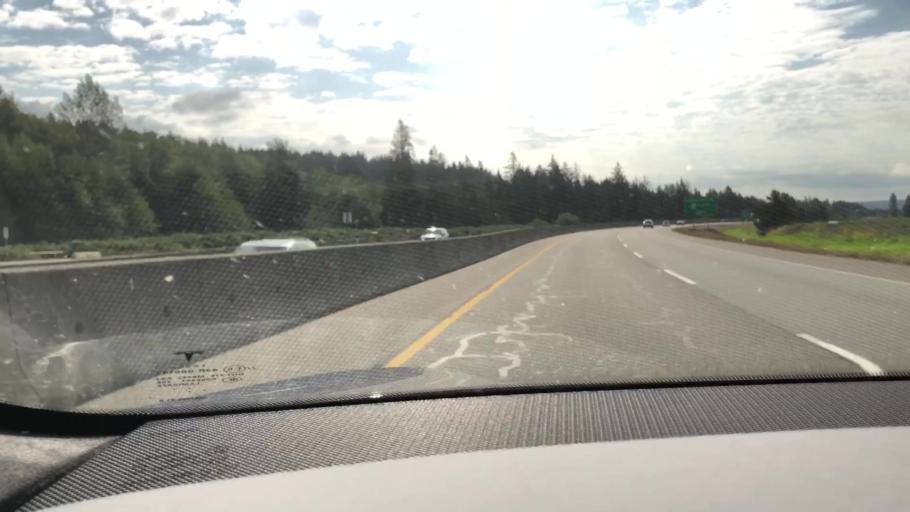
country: CA
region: British Columbia
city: Delta
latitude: 49.1115
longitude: -122.9075
